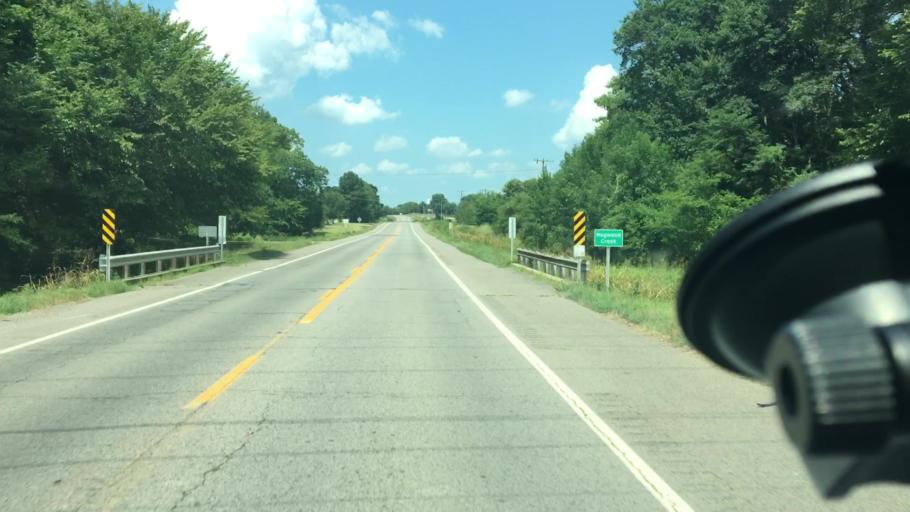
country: US
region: Arkansas
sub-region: Logan County
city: Paris
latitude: 35.2951
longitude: -93.6781
